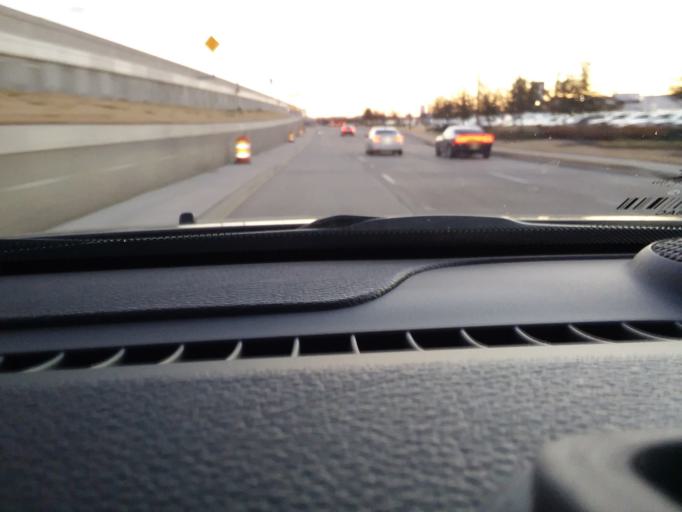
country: US
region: Texas
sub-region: Denton County
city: The Colony
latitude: 33.0613
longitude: -96.8274
